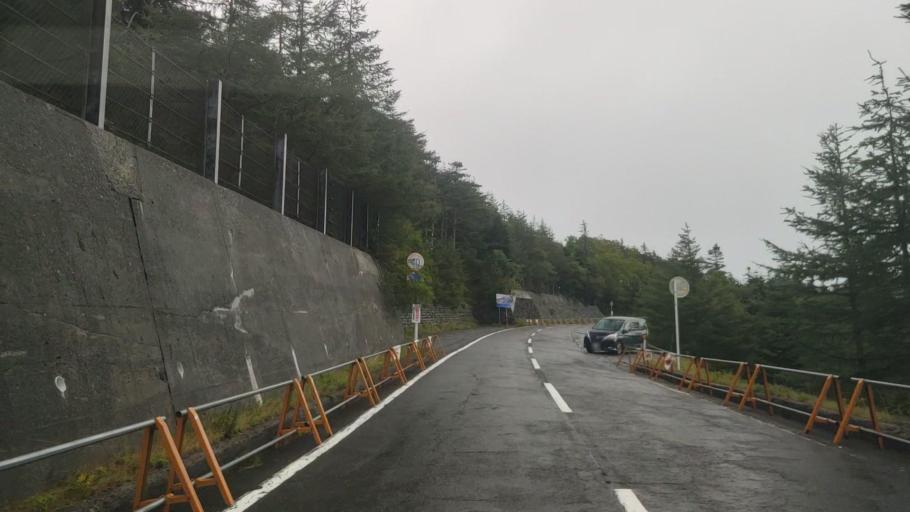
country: JP
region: Yamanashi
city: Fujikawaguchiko
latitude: 35.3366
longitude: 138.7310
